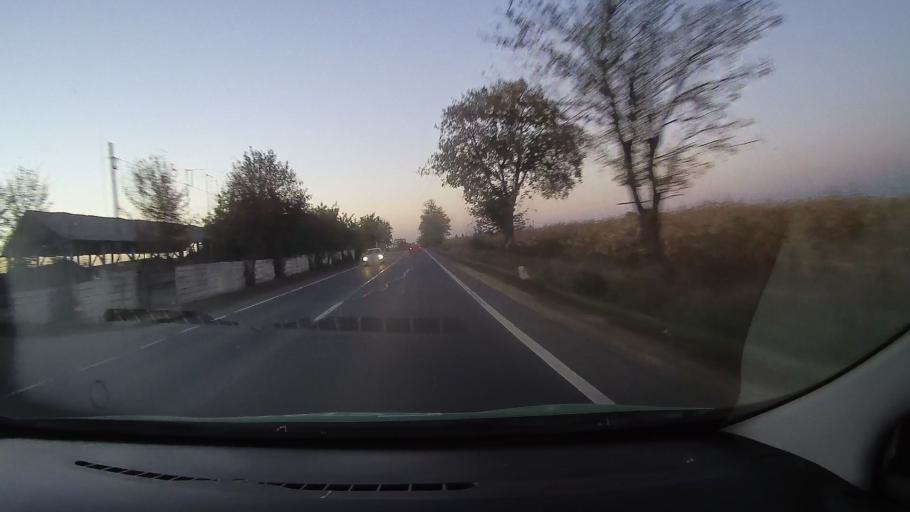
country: RO
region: Bihor
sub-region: Comuna Valea lui Mihai
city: Valea lui Mihai
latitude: 47.4999
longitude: 22.1485
